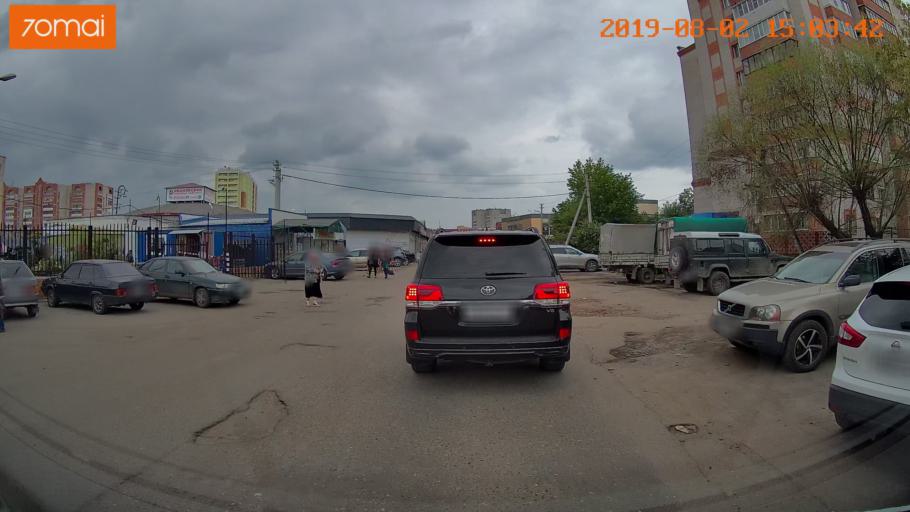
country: RU
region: Ivanovo
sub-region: Gorod Ivanovo
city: Ivanovo
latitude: 56.9897
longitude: 40.9664
